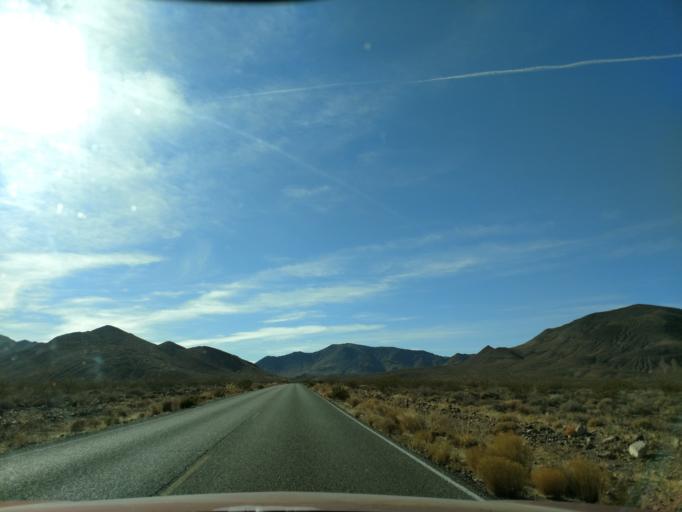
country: US
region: Nevada
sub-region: Nye County
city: Beatty
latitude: 36.8153
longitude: -116.9019
